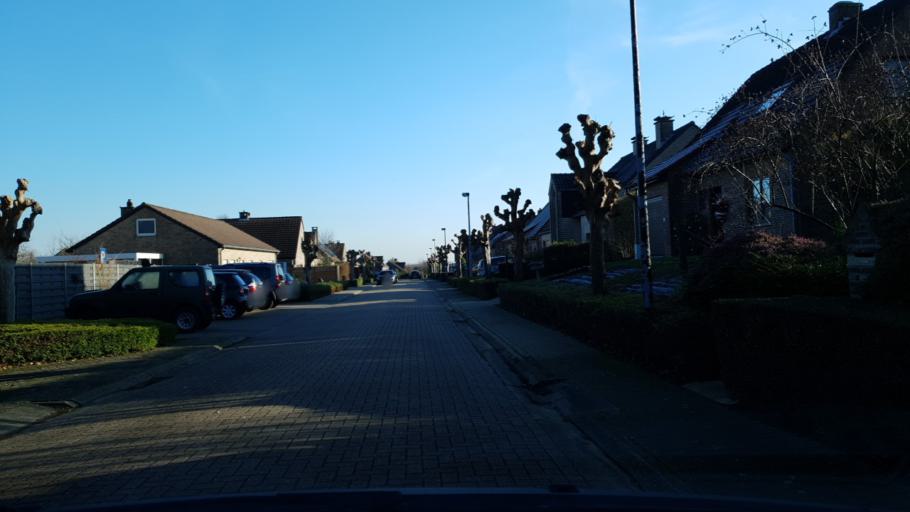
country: BE
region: Flanders
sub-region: Provincie Vlaams-Brabant
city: Bertem
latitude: 50.8726
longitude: 4.6244
